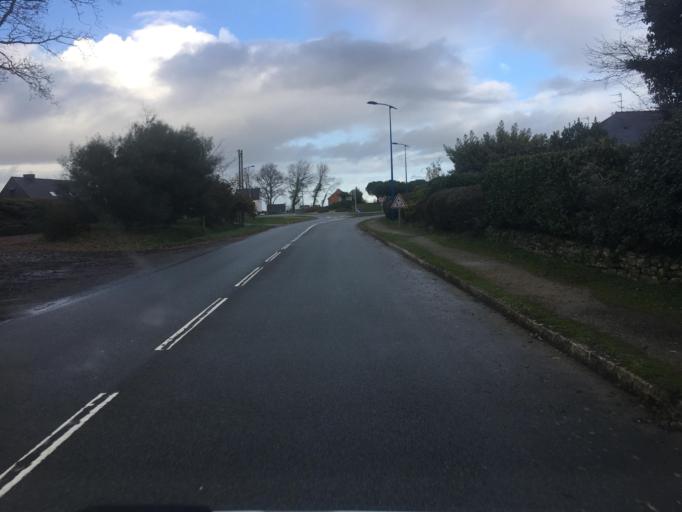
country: FR
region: Brittany
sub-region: Departement du Morbihan
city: Surzur
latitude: 47.5251
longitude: -2.6530
